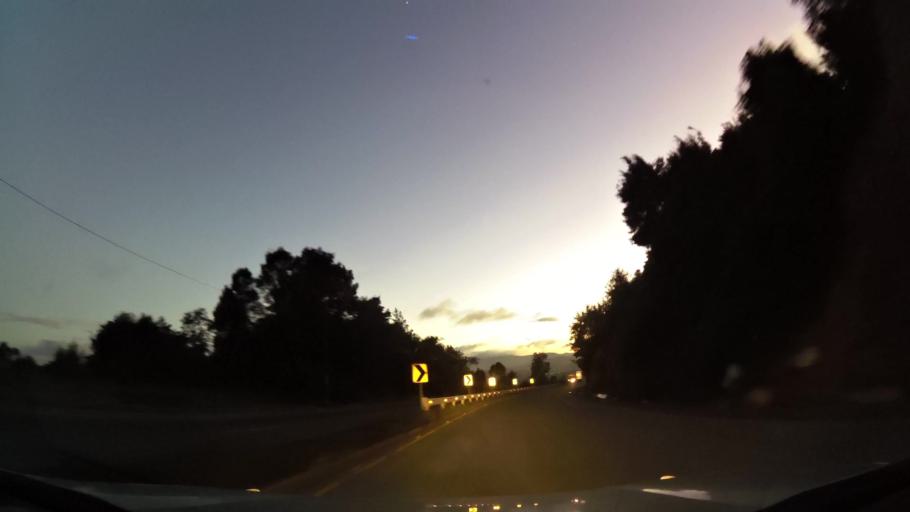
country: GT
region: Chimaltenango
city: Santa Apolonia
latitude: 14.7945
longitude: -90.9763
